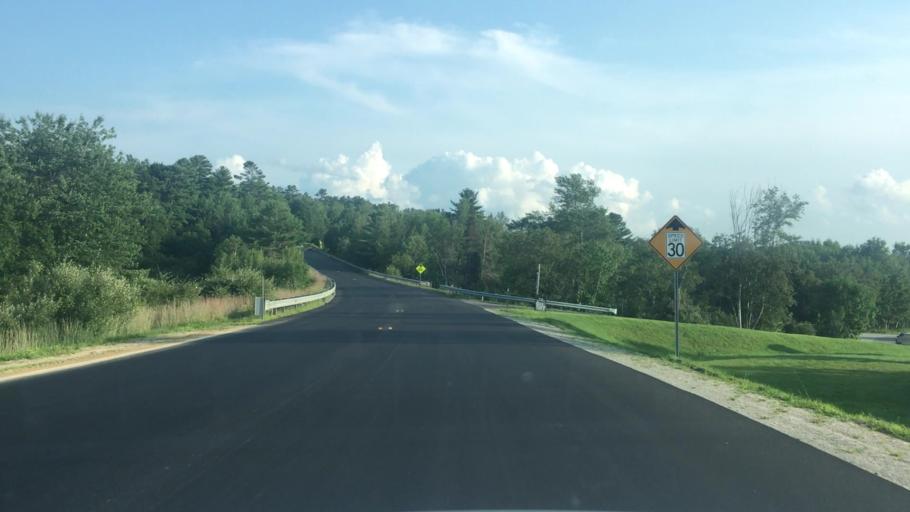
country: US
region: New Hampshire
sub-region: Sullivan County
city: Grantham
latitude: 43.5053
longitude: -72.1322
